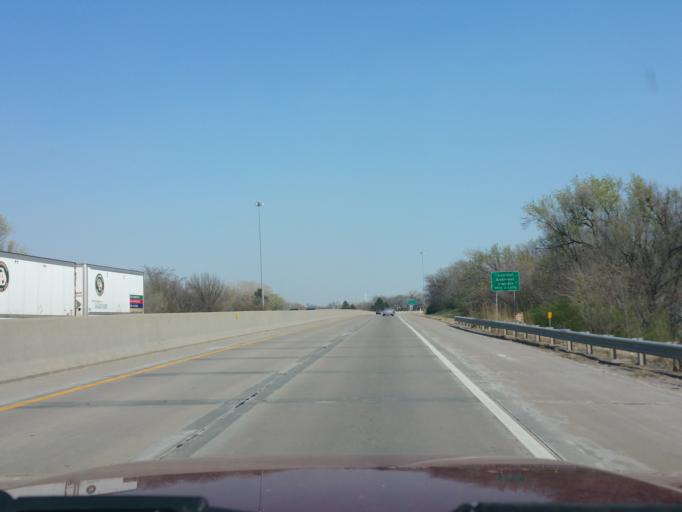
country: US
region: Kansas
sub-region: Shawnee County
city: Topeka
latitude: 39.0654
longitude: -95.6874
